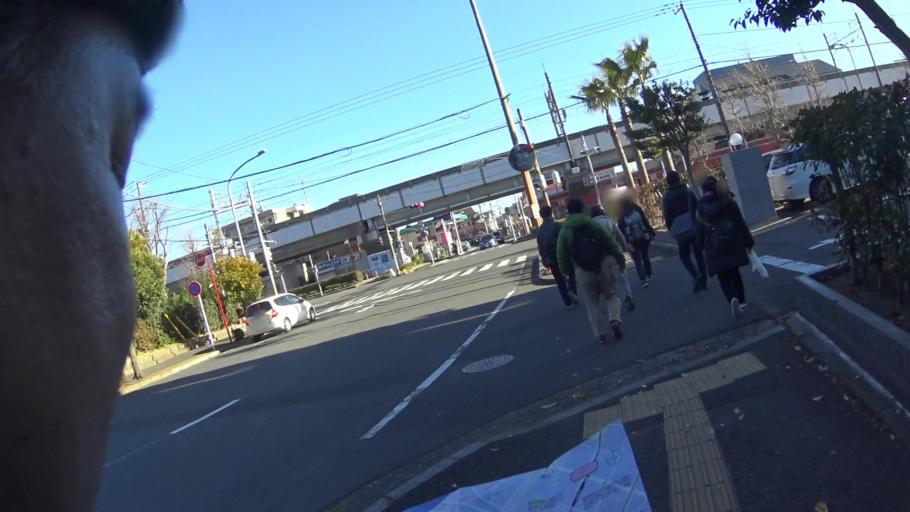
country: JP
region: Tokyo
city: Urayasu
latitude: 35.6440
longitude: 139.9046
